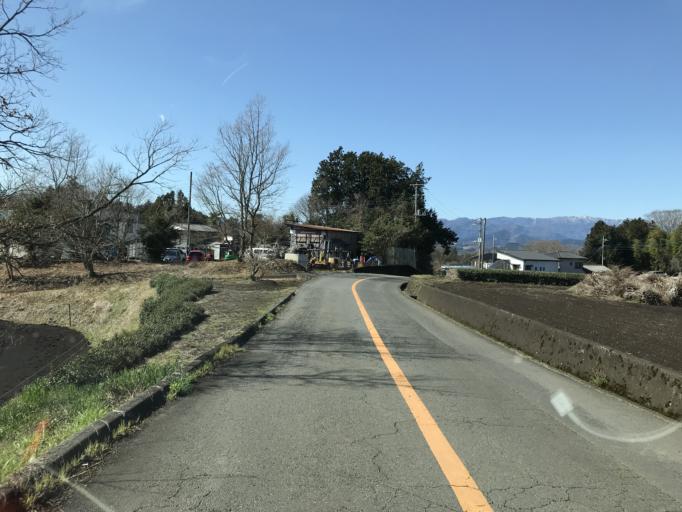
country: JP
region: Shizuoka
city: Fujinomiya
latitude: 35.2381
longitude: 138.6567
